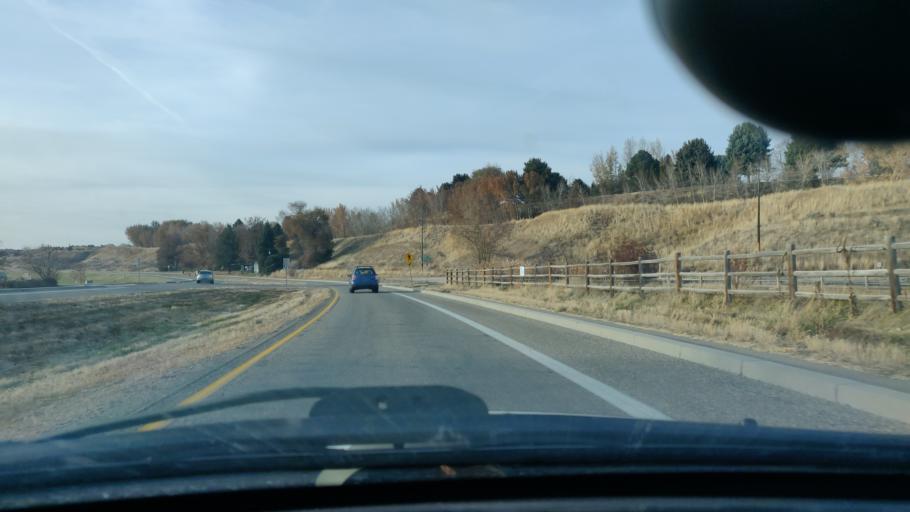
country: US
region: Idaho
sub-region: Ada County
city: Eagle
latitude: 43.6896
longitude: -116.3035
